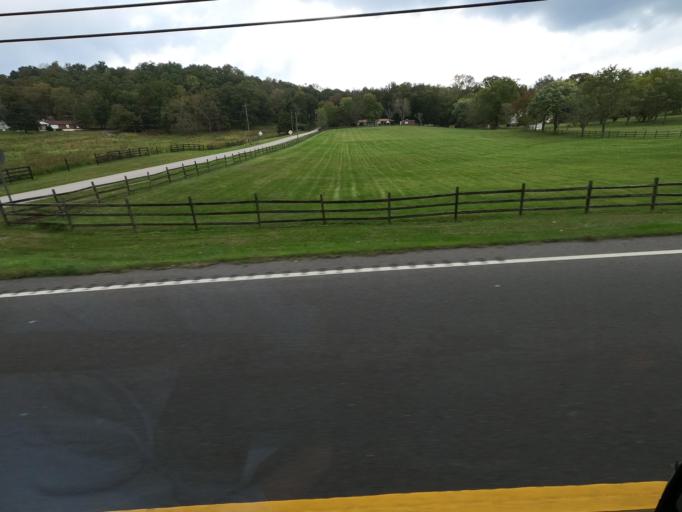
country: US
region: Tennessee
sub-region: Cheatham County
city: Pegram
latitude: 36.0972
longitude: -87.0322
